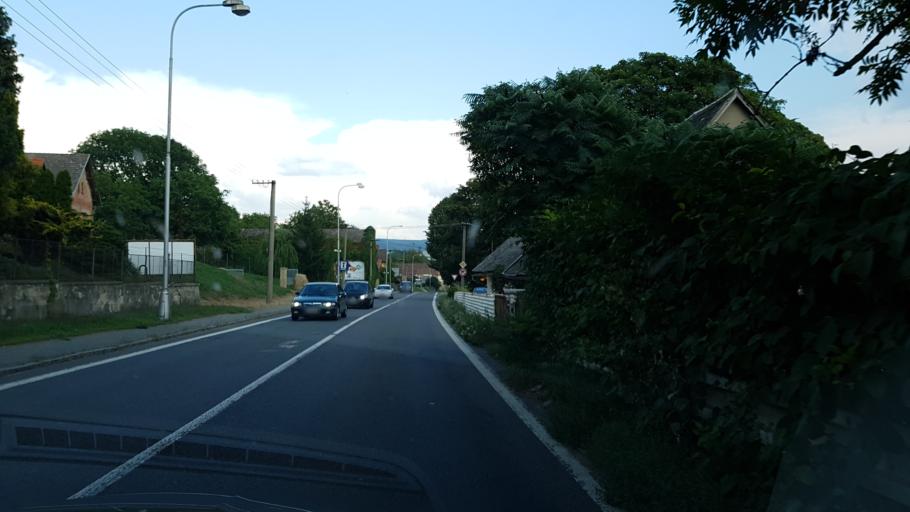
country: CZ
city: Doudleby nad Orlici
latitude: 50.1108
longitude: 16.2554
